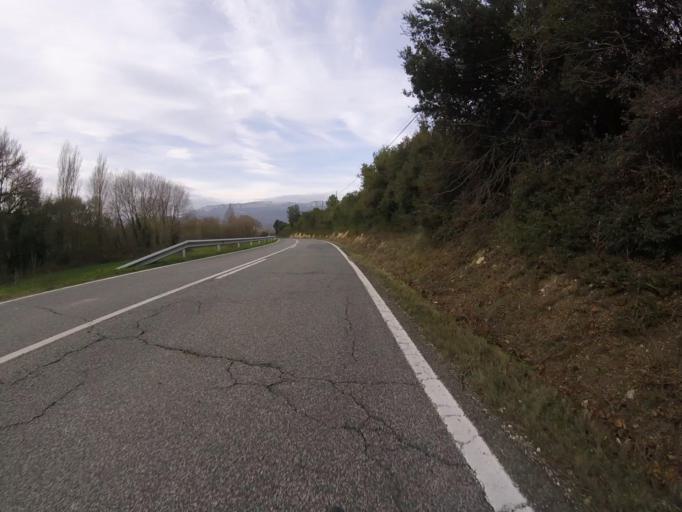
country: ES
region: Navarre
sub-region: Provincia de Navarra
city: Estella
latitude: 42.7027
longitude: -2.0619
